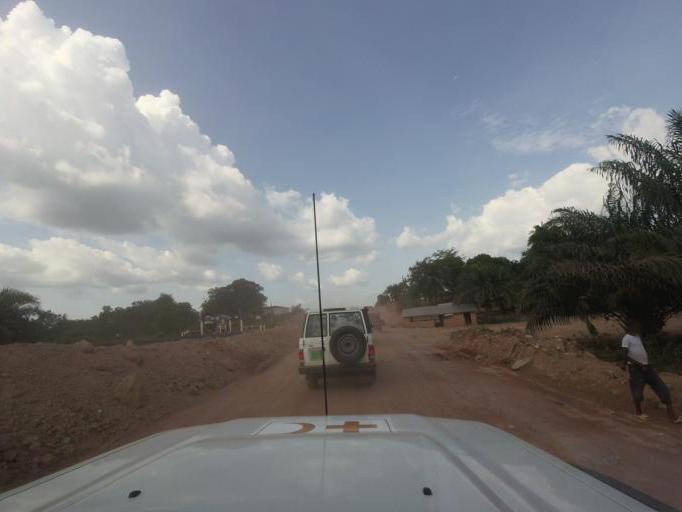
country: LR
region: Bong
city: Gbarnga
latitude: 7.0358
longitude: -9.5512
